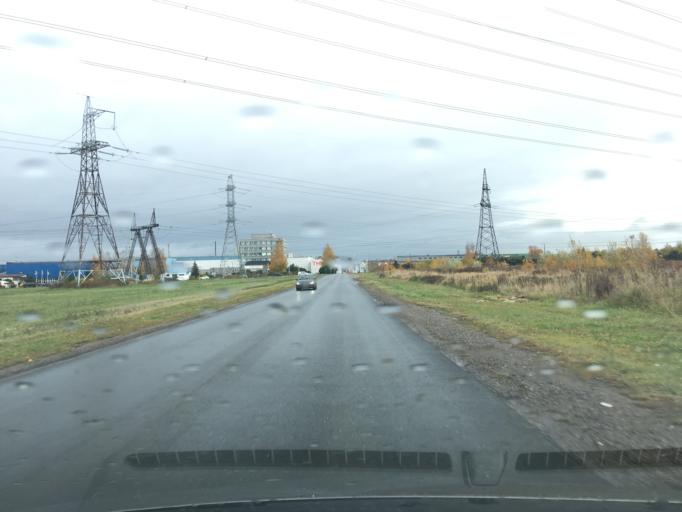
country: EE
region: Tartu
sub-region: Tartu linn
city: Tartu
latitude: 58.3801
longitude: 26.6812
